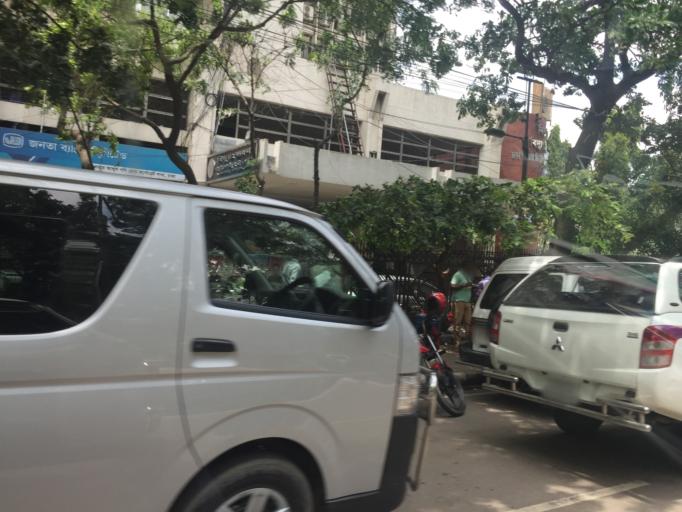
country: BD
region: Dhaka
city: Paltan
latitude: 23.7279
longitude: 90.4066
